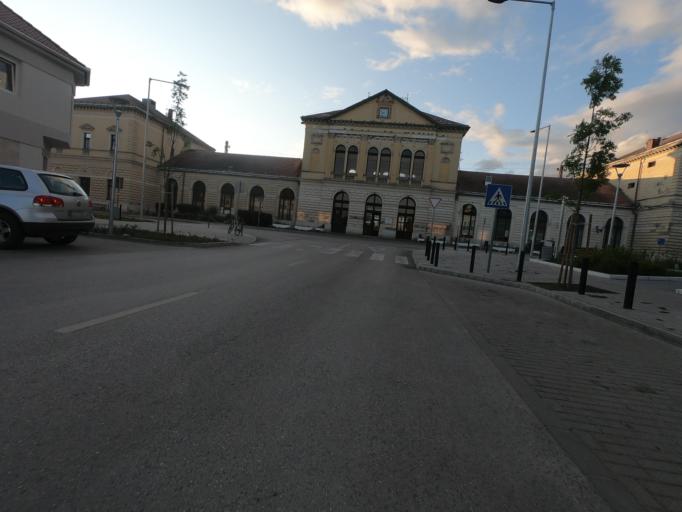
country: HU
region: Heves
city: Fuzesabony
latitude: 47.7509
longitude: 20.4167
